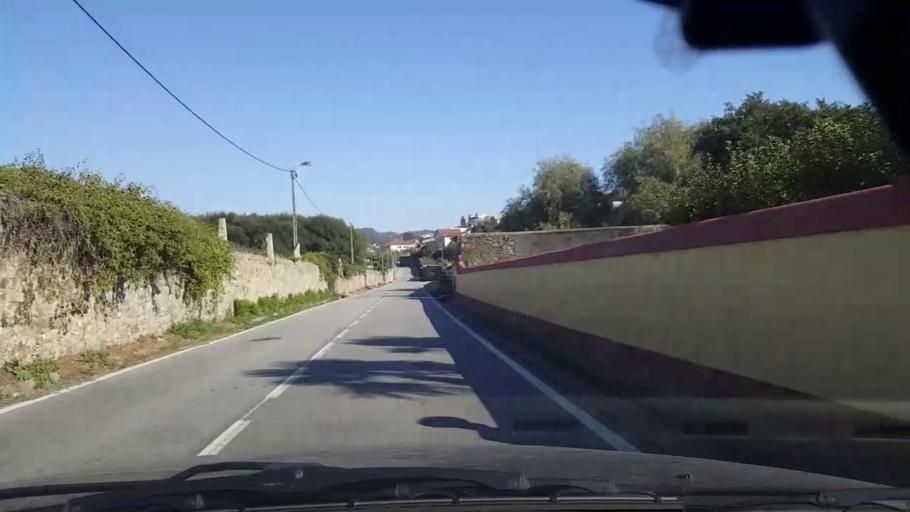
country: PT
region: Porto
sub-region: Vila do Conde
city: Arvore
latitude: 41.3347
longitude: -8.6709
